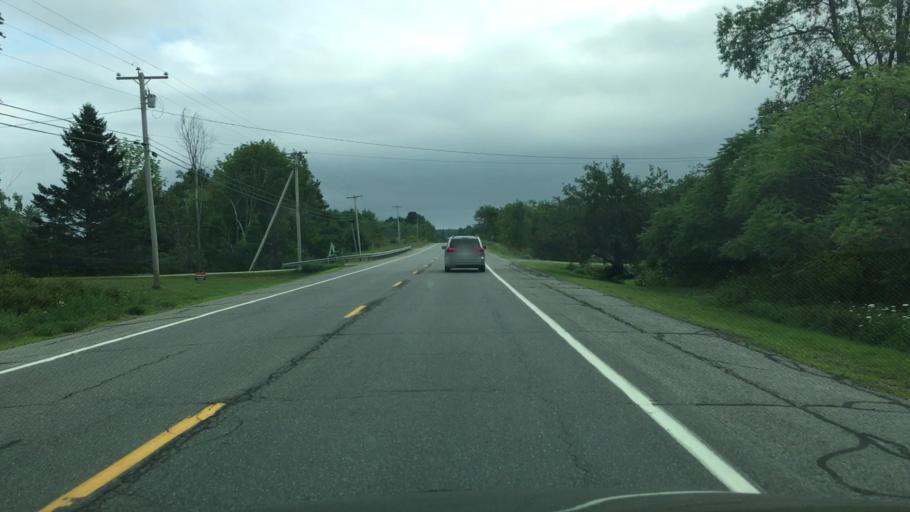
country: US
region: Maine
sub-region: Waldo County
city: Stockton Springs
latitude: 44.5351
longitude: -68.8611
